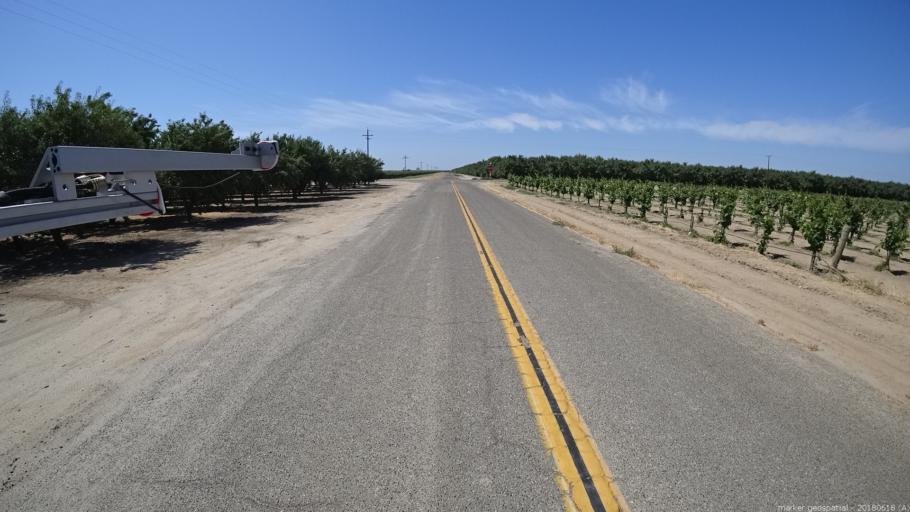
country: US
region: California
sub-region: Madera County
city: Parkwood
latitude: 36.8518
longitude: -120.1828
